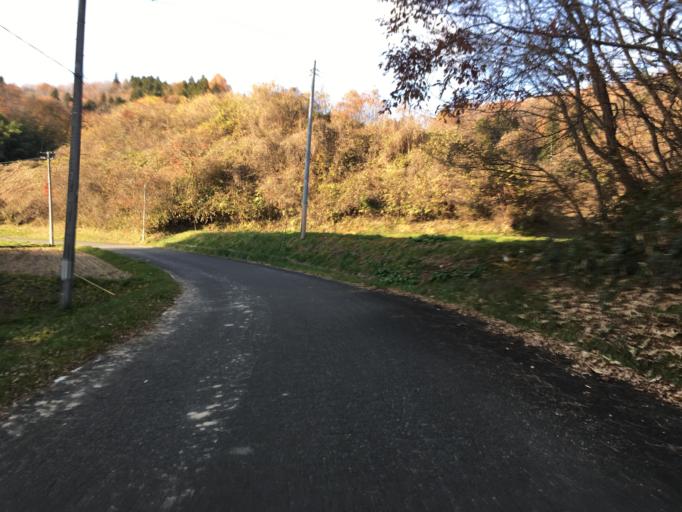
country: JP
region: Fukushima
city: Ishikawa
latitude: 37.2489
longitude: 140.5806
